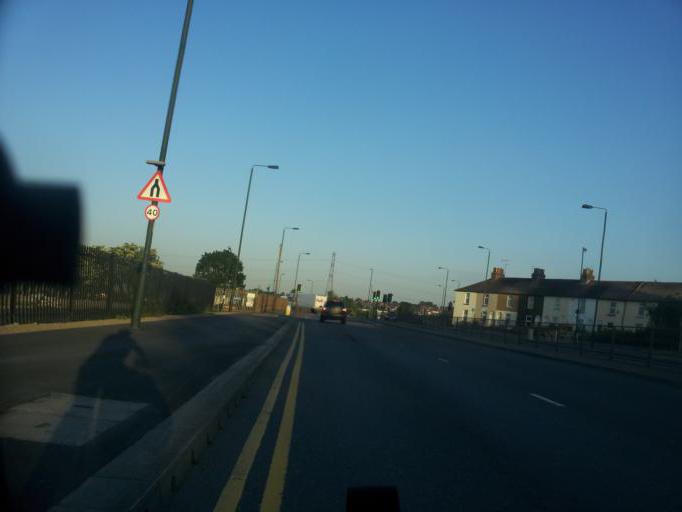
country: GB
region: England
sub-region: Kent
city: Dartford
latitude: 51.4574
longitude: 0.1948
